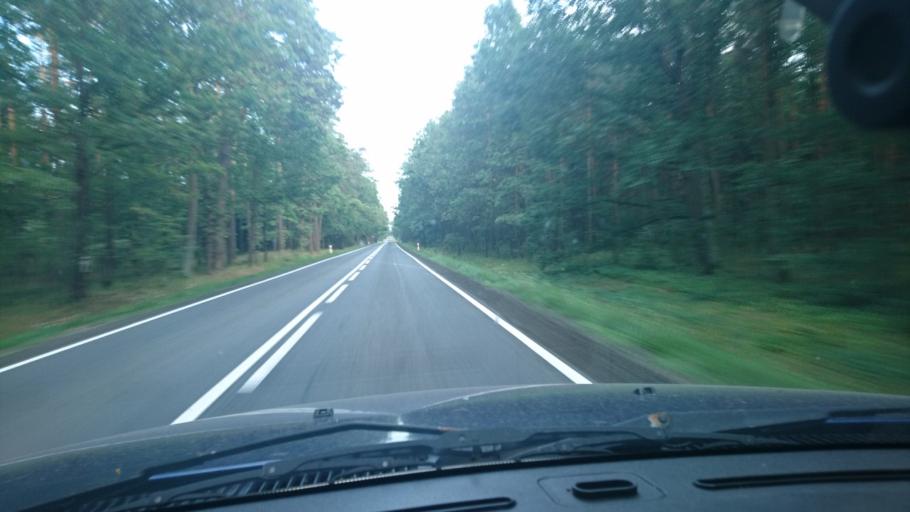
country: PL
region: Opole Voivodeship
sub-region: Powiat oleski
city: Olesno
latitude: 50.8499
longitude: 18.4708
